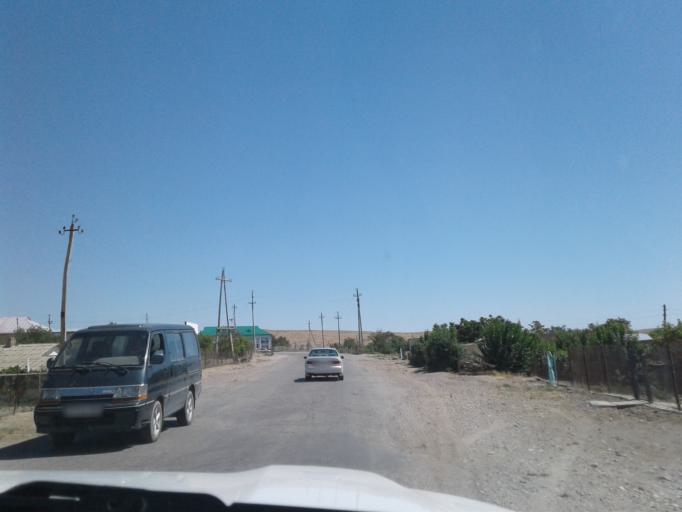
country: AF
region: Badghis
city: Bala Murghab
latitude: 35.9557
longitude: 62.9053
